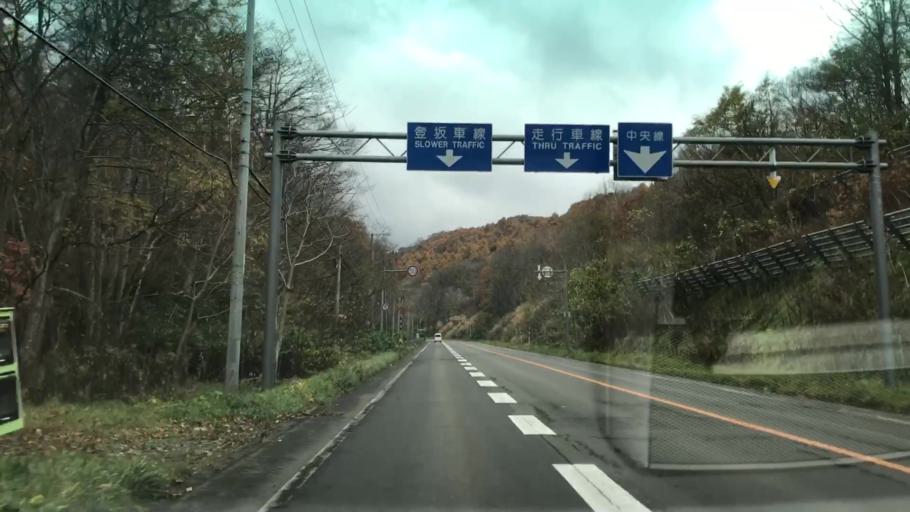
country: JP
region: Hokkaido
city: Yoichi
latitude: 43.2272
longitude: 140.7345
